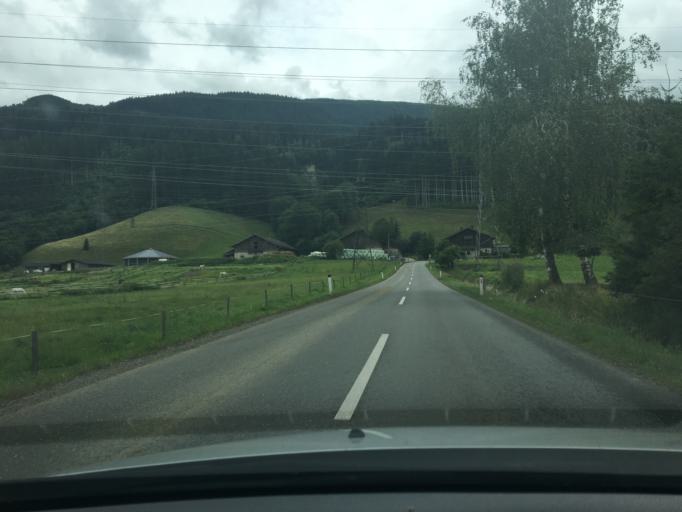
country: AT
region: Salzburg
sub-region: Politischer Bezirk Zell am See
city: Kaprun
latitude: 47.2811
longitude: 12.7844
